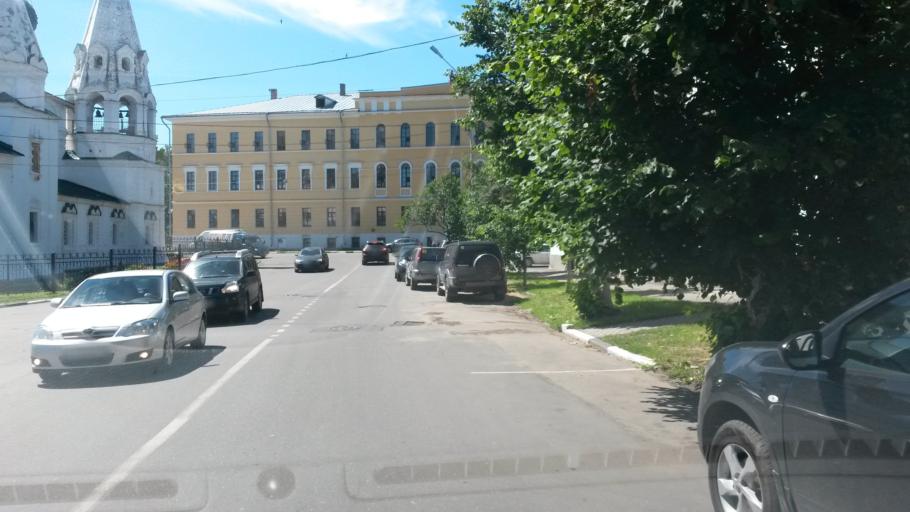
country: RU
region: Jaroslavl
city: Yaroslavl
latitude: 57.6231
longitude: 39.8963
